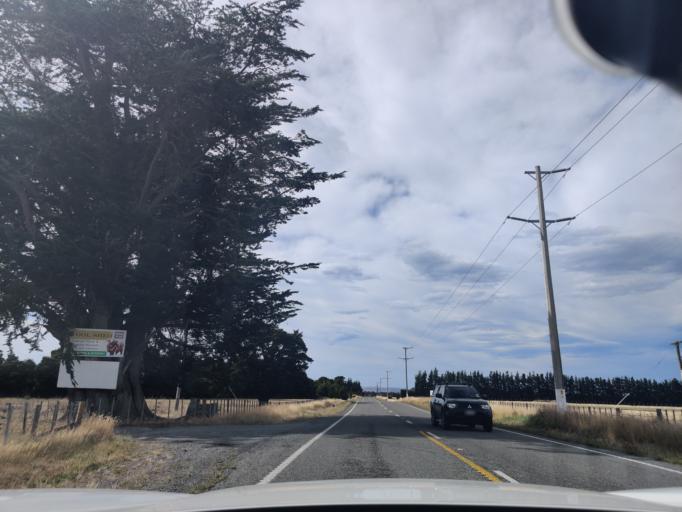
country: NZ
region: Wellington
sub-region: Masterton District
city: Masterton
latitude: -40.8362
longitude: 175.6293
